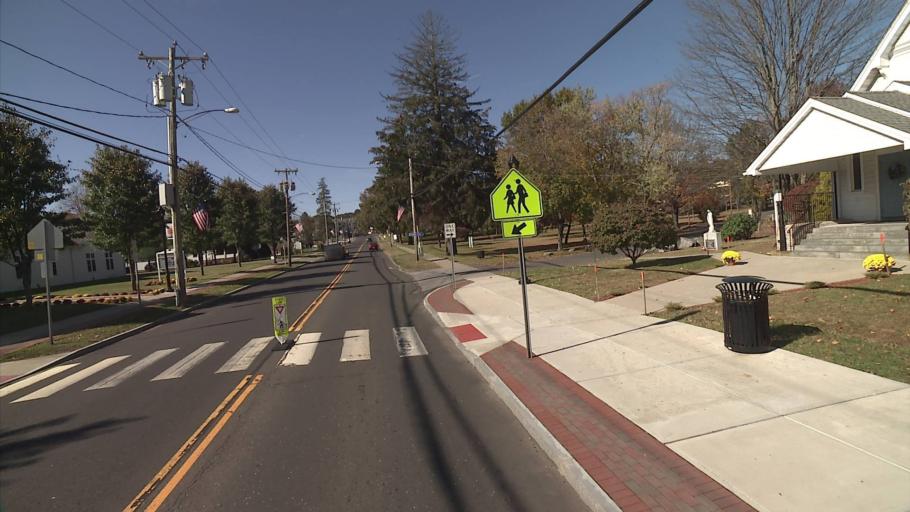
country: US
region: Connecticut
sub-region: Litchfield County
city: Terryville
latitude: 41.6784
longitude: -73.0076
